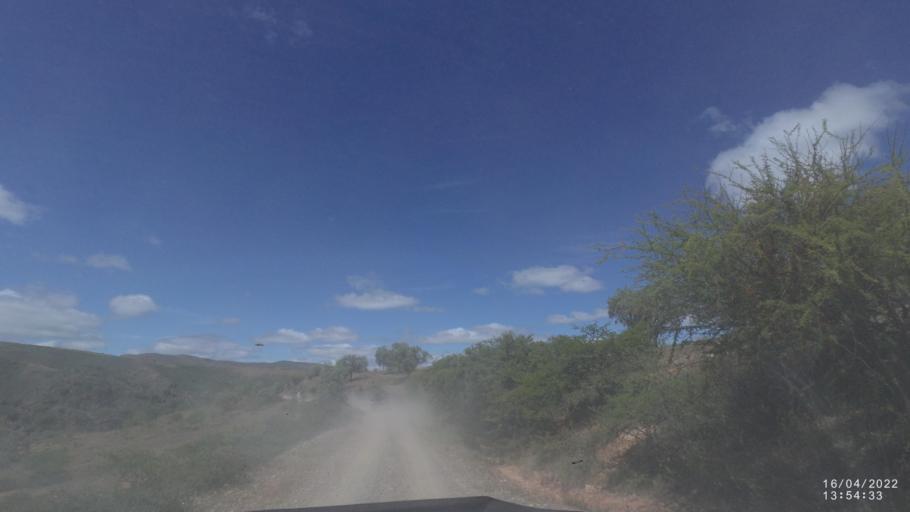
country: BO
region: Cochabamba
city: Mizque
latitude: -18.0259
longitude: -65.5650
